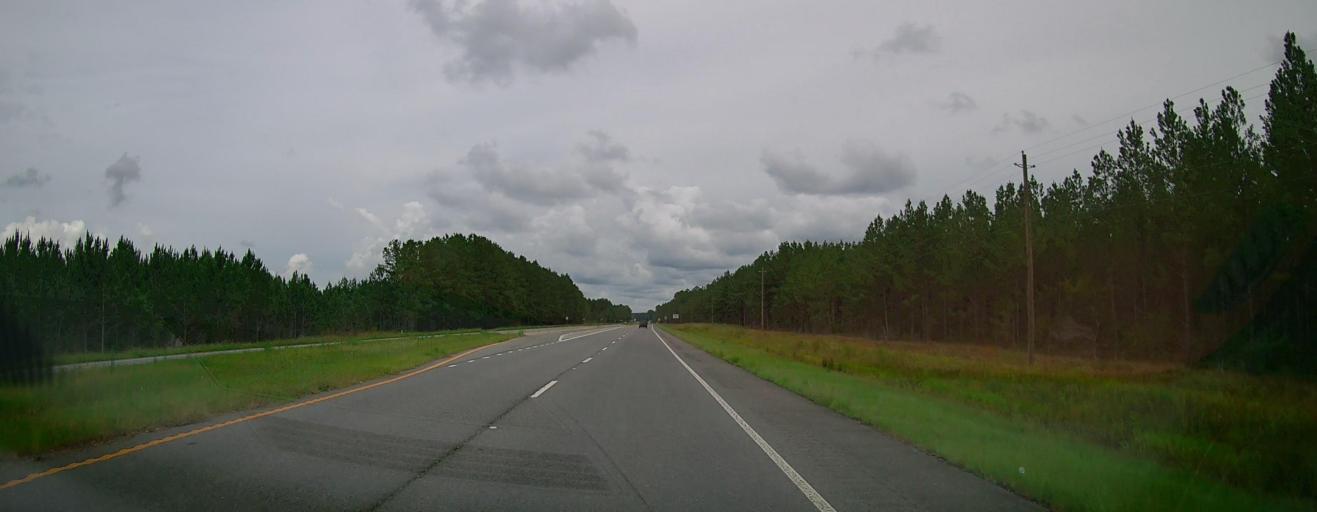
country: US
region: Georgia
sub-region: Appling County
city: Baxley
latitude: 31.7314
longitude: -82.2138
